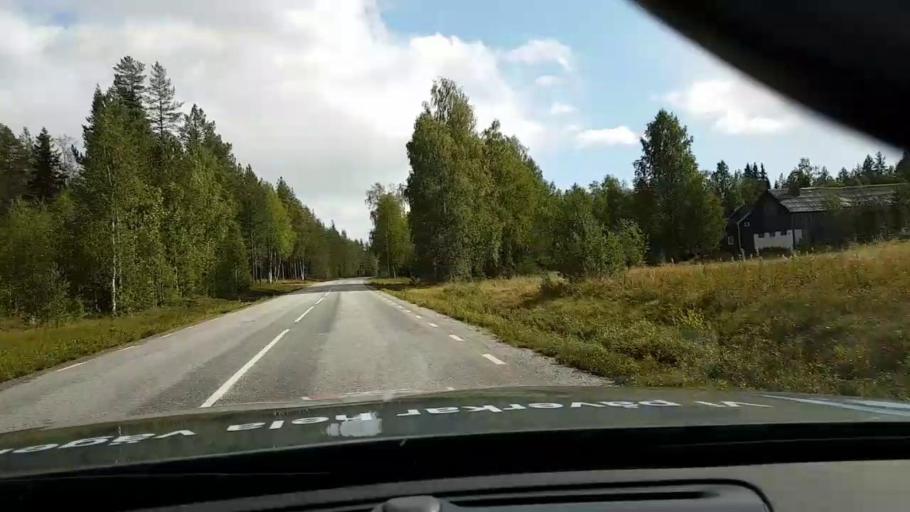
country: SE
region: Vaesternorrland
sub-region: OErnskoeldsviks Kommun
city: Bredbyn
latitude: 63.6495
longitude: 17.8917
